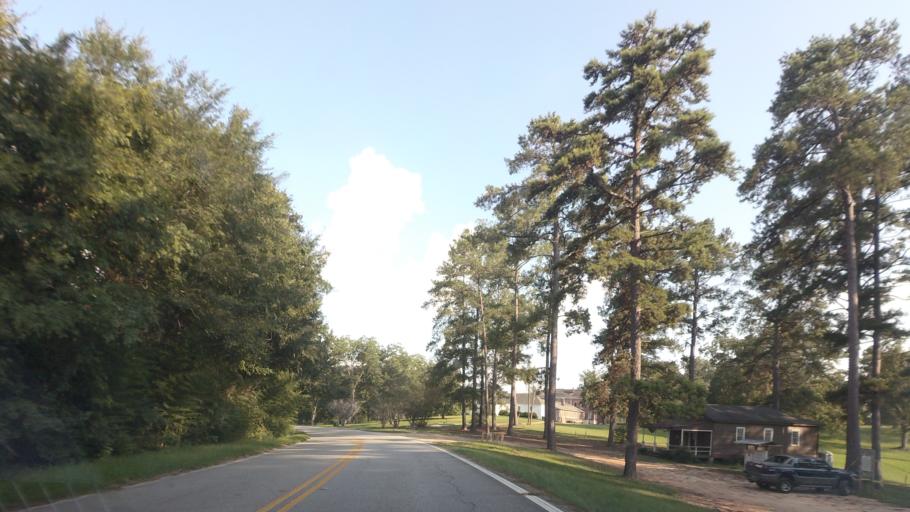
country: US
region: Georgia
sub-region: Bibb County
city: Macon
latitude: 32.8478
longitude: -83.7150
